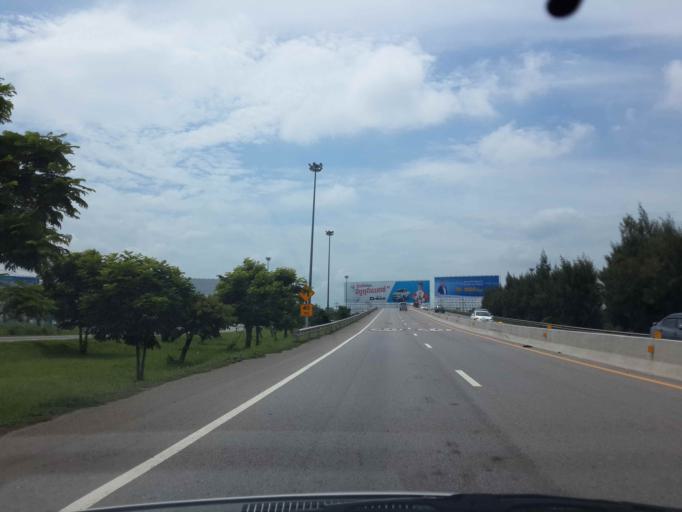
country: TH
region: Ratchaburi
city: Pak Tho
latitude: 13.3407
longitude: 99.8333
